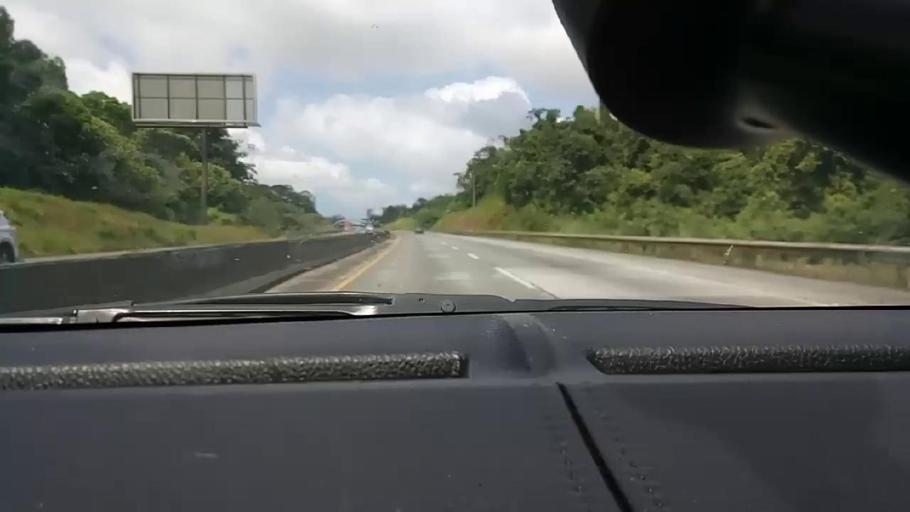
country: PA
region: Colon
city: Rio Rita
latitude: 9.2967
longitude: -79.7867
